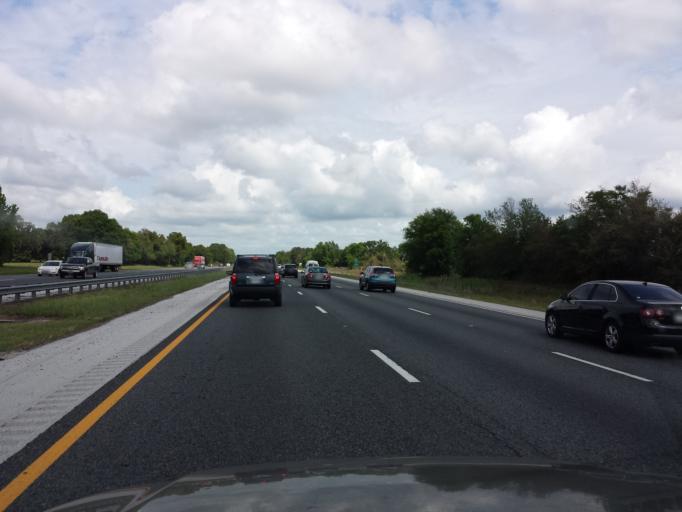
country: US
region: Florida
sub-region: Marion County
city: Citra
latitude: 29.4483
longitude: -82.2675
